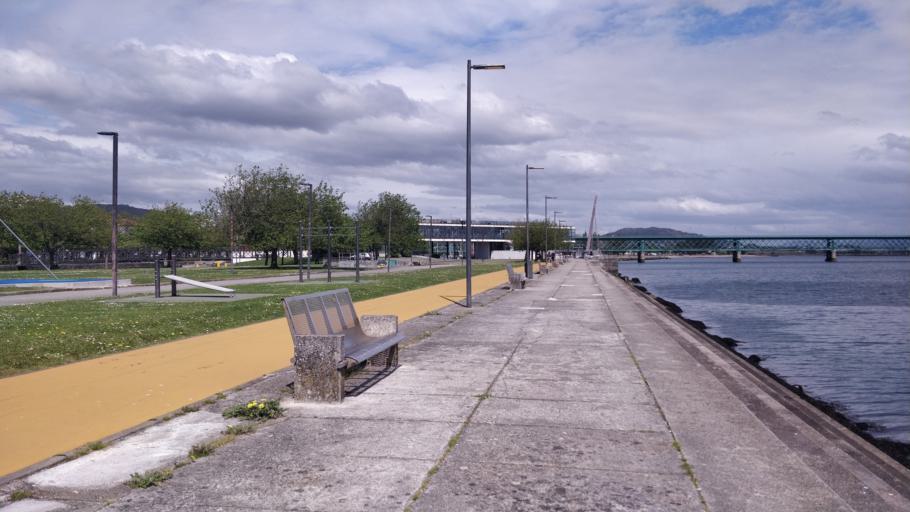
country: PT
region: Viana do Castelo
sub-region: Viana do Castelo
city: Viana do Castelo
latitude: 41.6921
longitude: -8.8248
